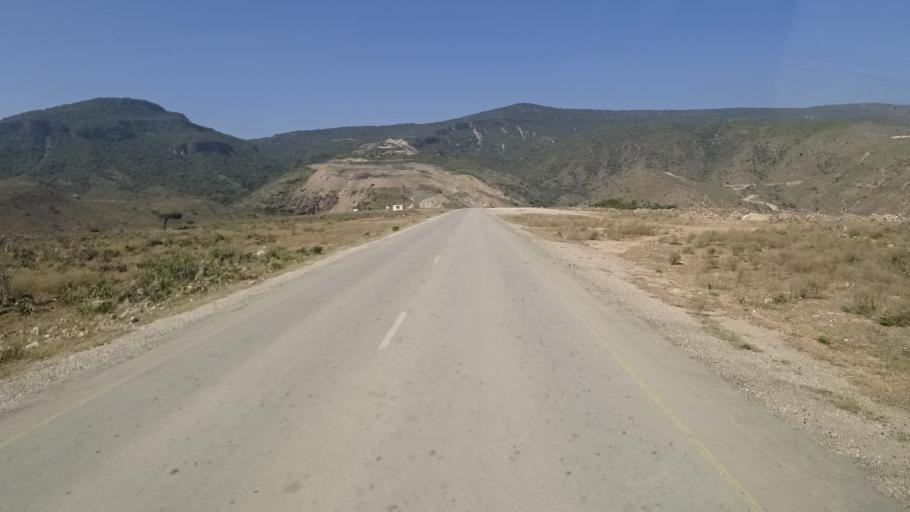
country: OM
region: Zufar
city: Salalah
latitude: 17.0368
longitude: 54.6128
